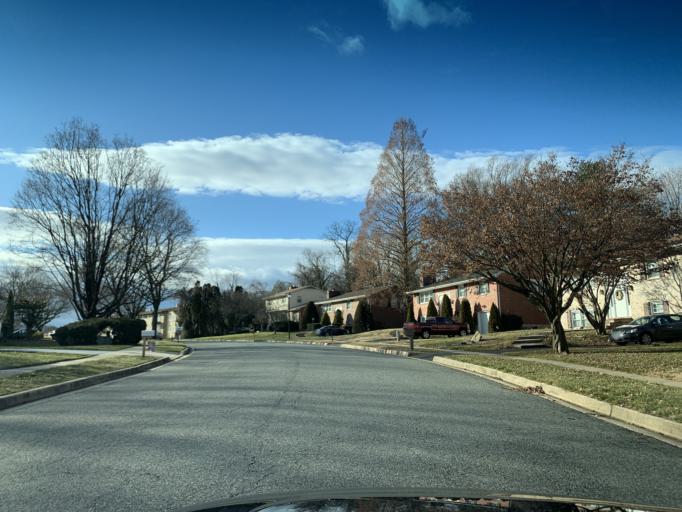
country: US
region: Maryland
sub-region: Harford County
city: South Bel Air
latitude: 39.5309
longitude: -76.3381
